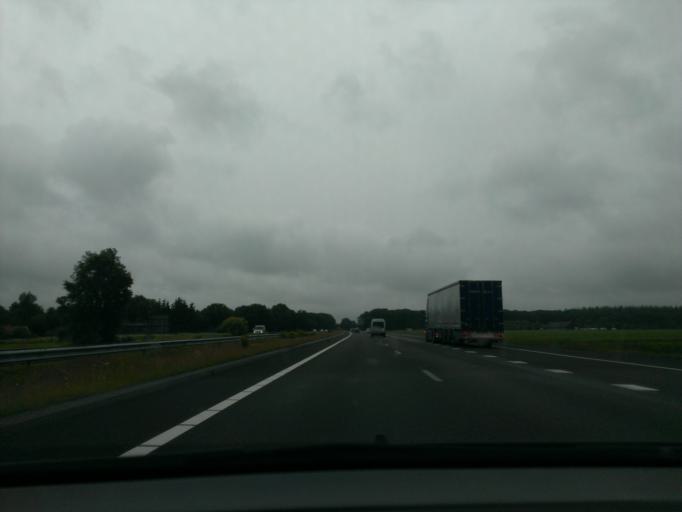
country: NL
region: Drenthe
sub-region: Gemeente Westerveld
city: Dwingeloo
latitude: 52.8422
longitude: 6.4844
